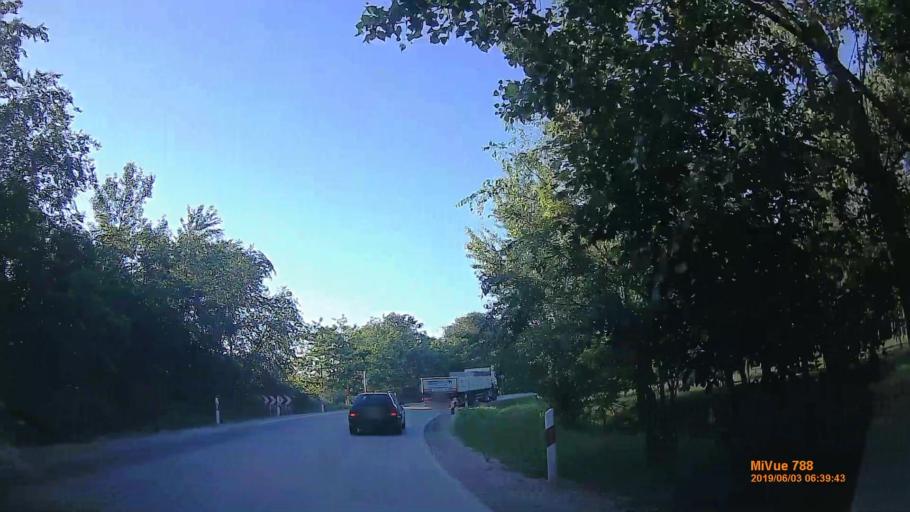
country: HU
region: Pest
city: Dunavarsany
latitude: 47.2851
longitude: 19.1039
